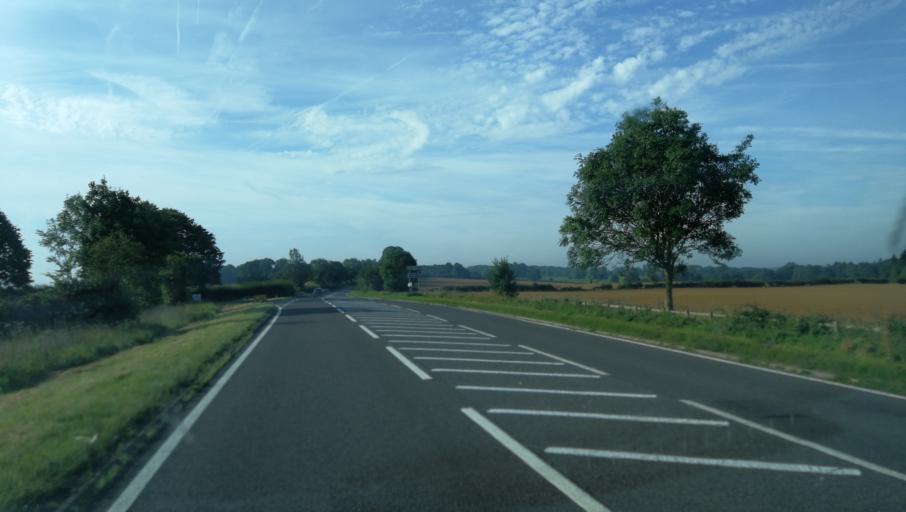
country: GB
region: England
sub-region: Oxfordshire
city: Deddington
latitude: 51.9301
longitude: -1.3254
